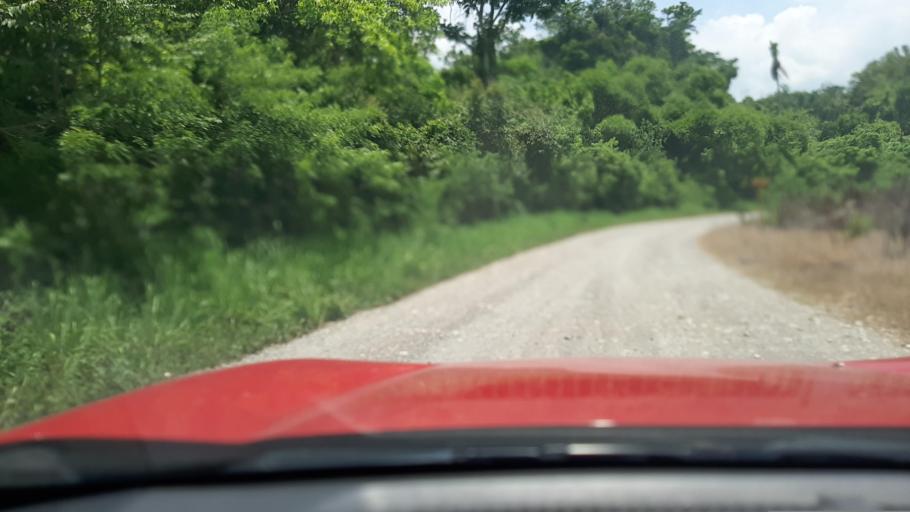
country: MX
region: Veracruz
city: Papantla de Olarte
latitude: 20.4229
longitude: -97.2649
